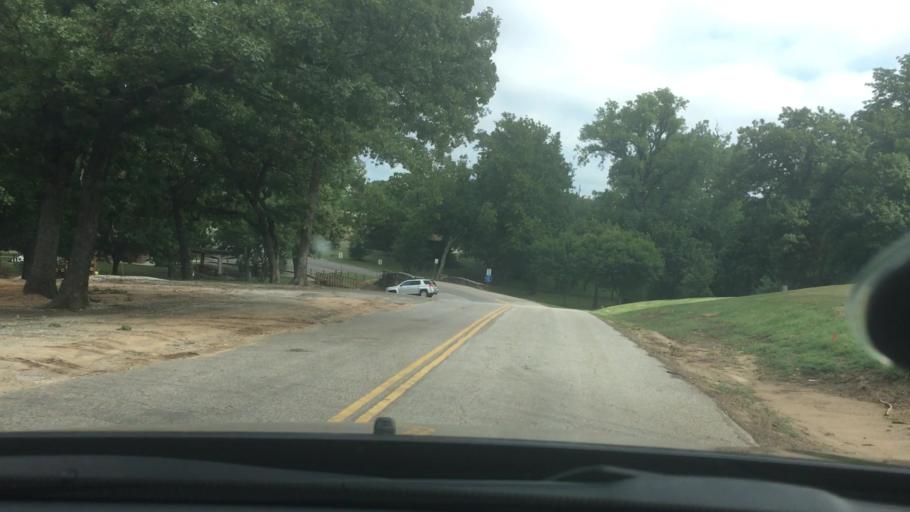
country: US
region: Oklahoma
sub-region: Pontotoc County
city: Ada
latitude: 34.7644
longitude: -96.6521
